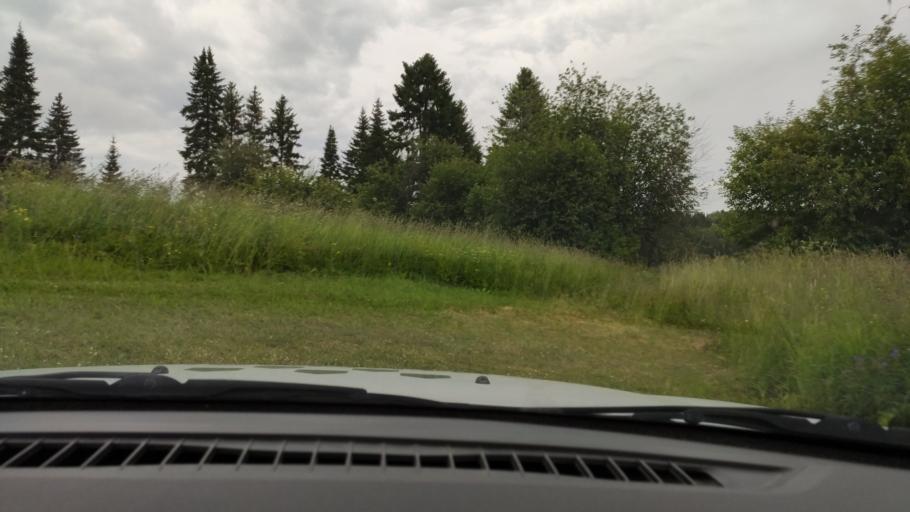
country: RU
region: Perm
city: Orda
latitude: 57.2942
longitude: 56.5772
